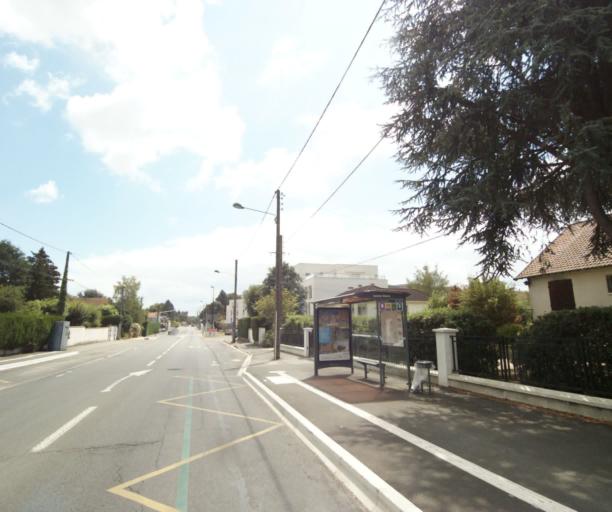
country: FR
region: Centre
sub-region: Departement du Loiret
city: Saint-Jean-de-Braye
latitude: 47.9076
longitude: 1.9805
